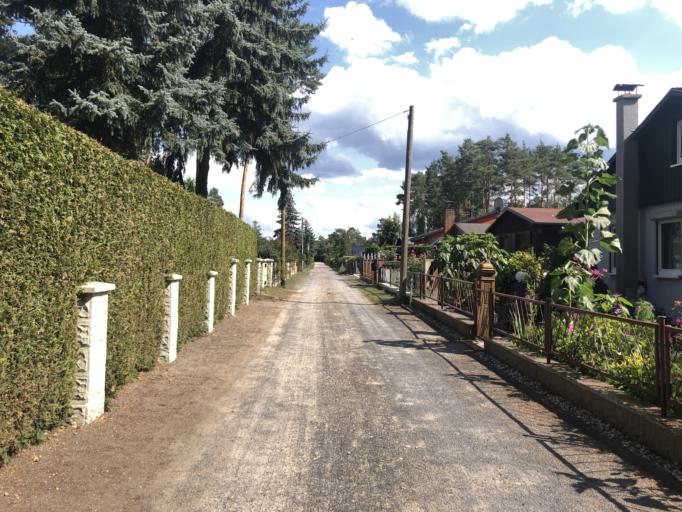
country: DE
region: Brandenburg
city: Mullrose
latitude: 52.2350
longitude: 14.4063
